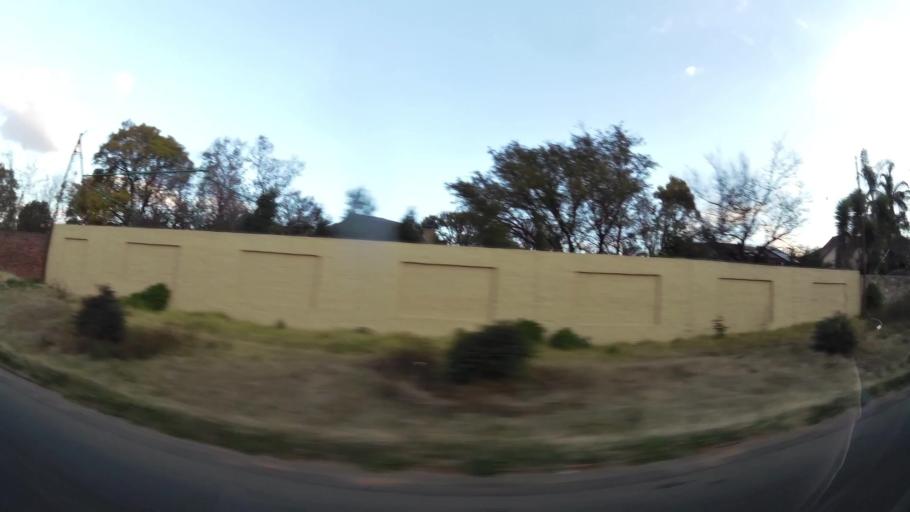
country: ZA
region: Gauteng
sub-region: West Rand District Municipality
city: Krugersdorp
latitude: -26.0762
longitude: 27.7882
